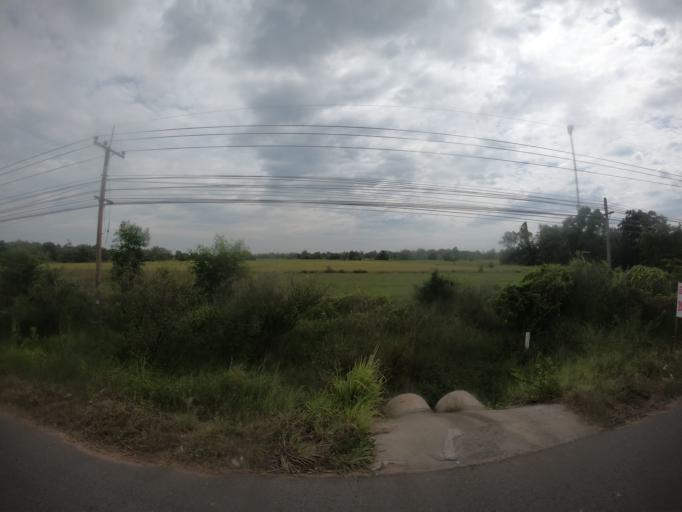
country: TH
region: Maha Sarakham
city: Kantharawichai
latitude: 16.2800
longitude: 103.2908
